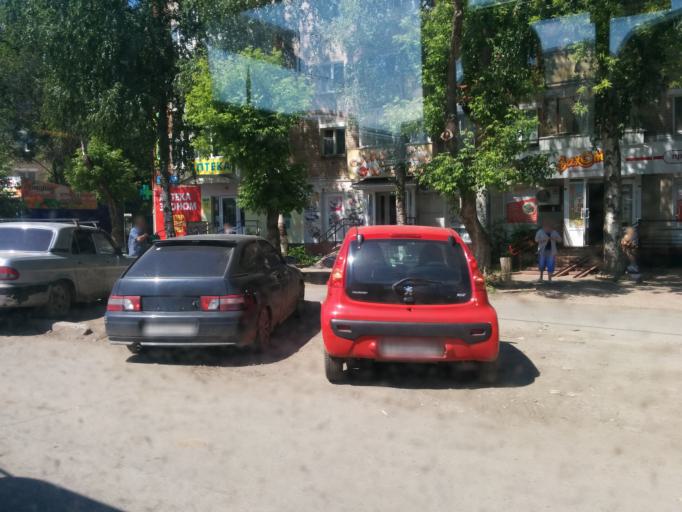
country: RU
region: Perm
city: Perm
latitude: 57.9986
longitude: 56.2942
